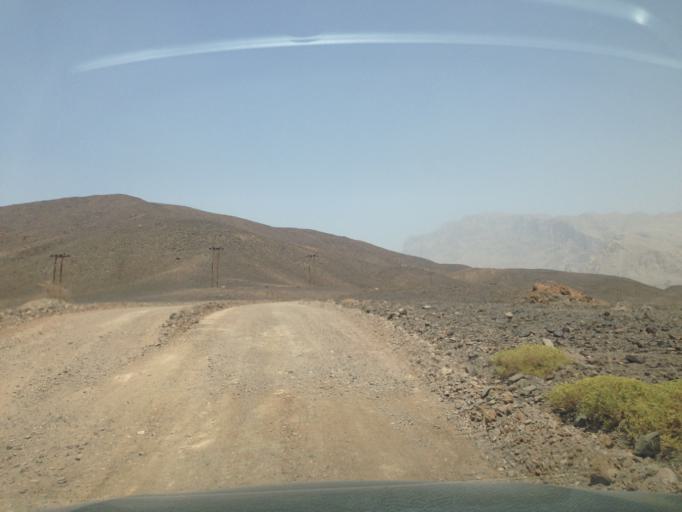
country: OM
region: Az Zahirah
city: `Ibri
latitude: 23.1990
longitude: 56.8796
